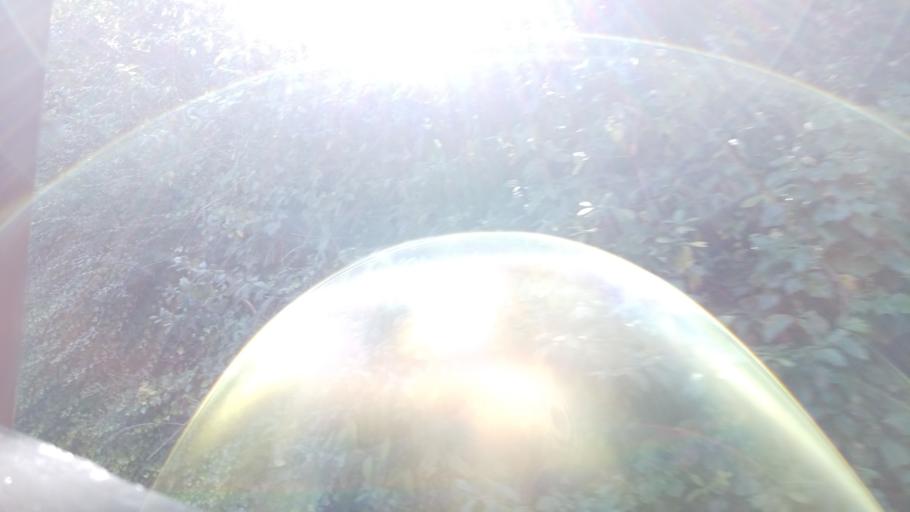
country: US
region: California
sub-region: Mendocino County
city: Fort Bragg
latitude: 39.4502
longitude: -123.7990
